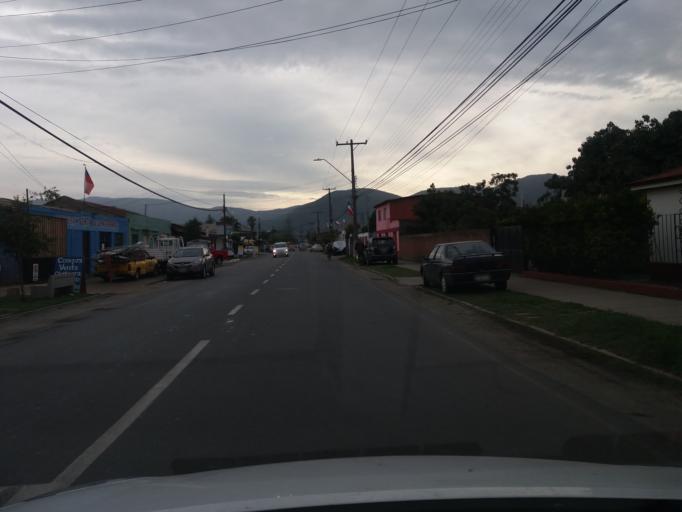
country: CL
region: Valparaiso
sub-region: Provincia de Quillota
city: Hacienda La Calera
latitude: -32.7783
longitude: -71.1885
